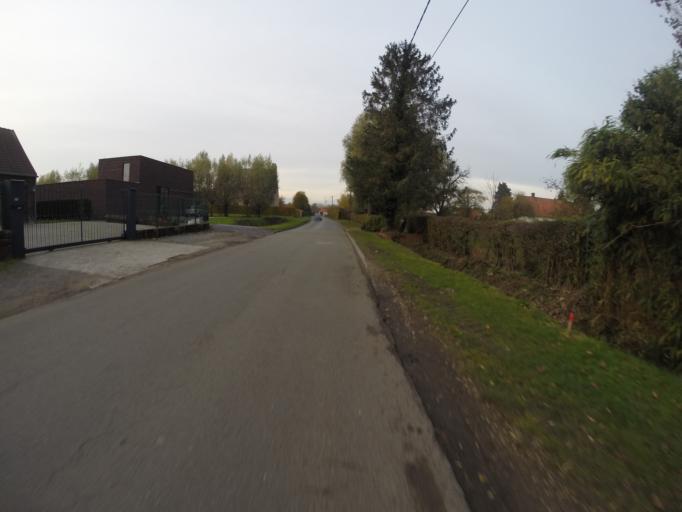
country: BE
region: Flanders
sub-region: Provincie Oost-Vlaanderen
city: Aalter
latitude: 51.1023
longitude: 3.4674
